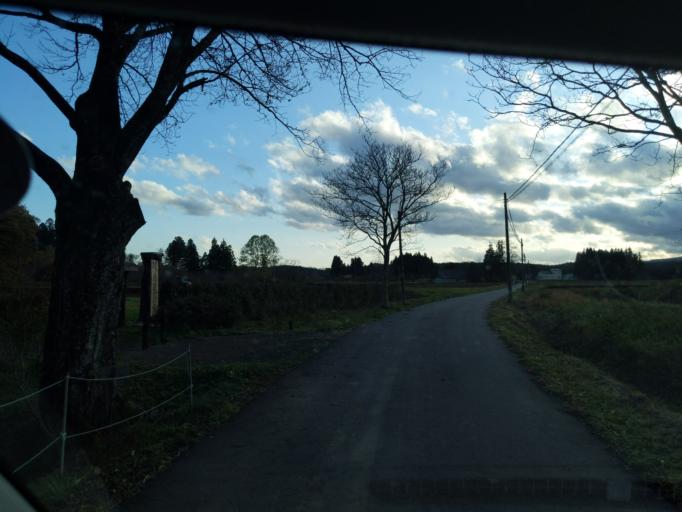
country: JP
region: Iwate
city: Mizusawa
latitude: 39.0870
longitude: 141.0358
